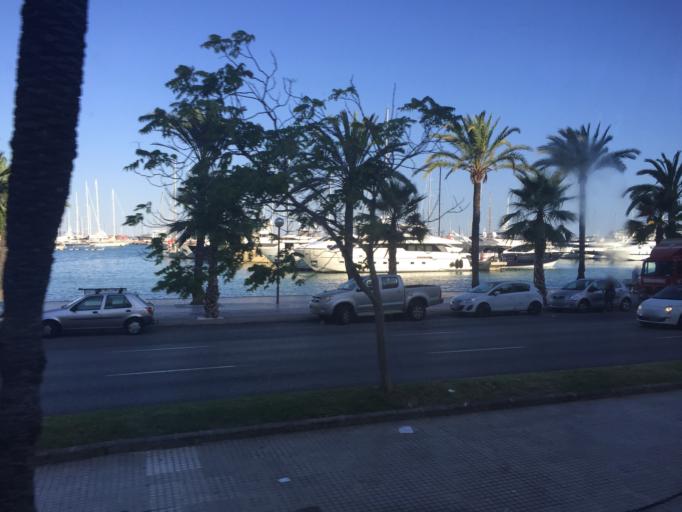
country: ES
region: Balearic Islands
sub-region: Illes Balears
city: Palma
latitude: 39.5660
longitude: 2.6287
